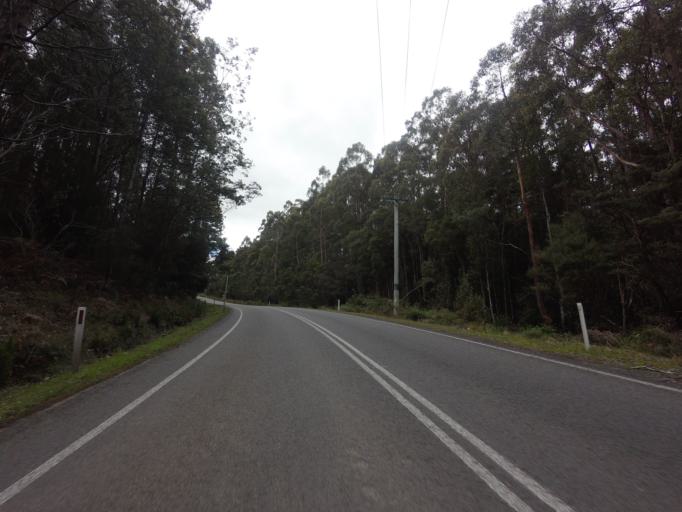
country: AU
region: Tasmania
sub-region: Huon Valley
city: Geeveston
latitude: -43.4038
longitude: 146.9574
